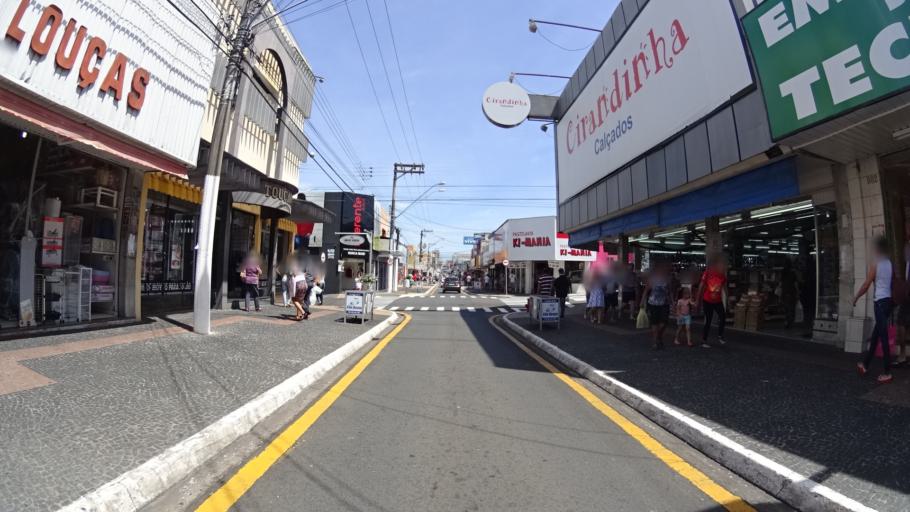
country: BR
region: Sao Paulo
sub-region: Marilia
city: Marilia
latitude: -22.2150
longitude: -49.9513
